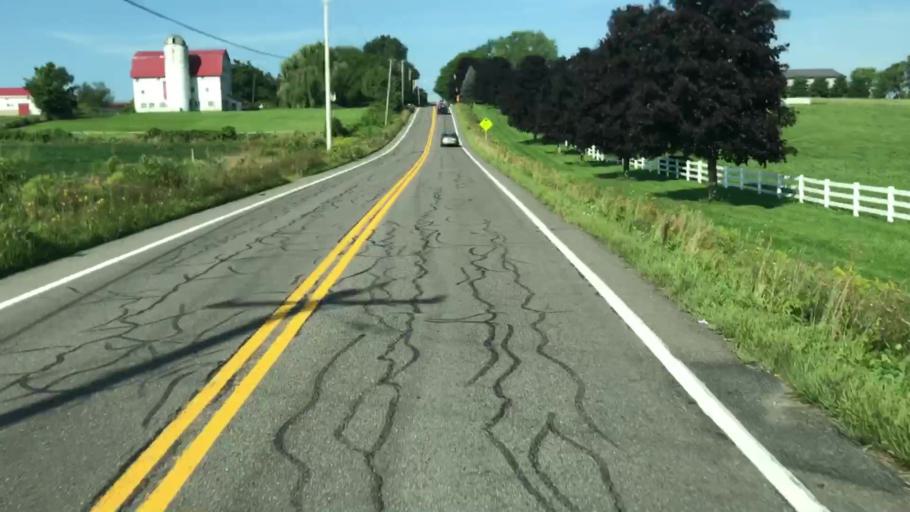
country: US
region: New York
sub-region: Onondaga County
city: Skaneateles
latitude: 42.9587
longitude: -76.4513
